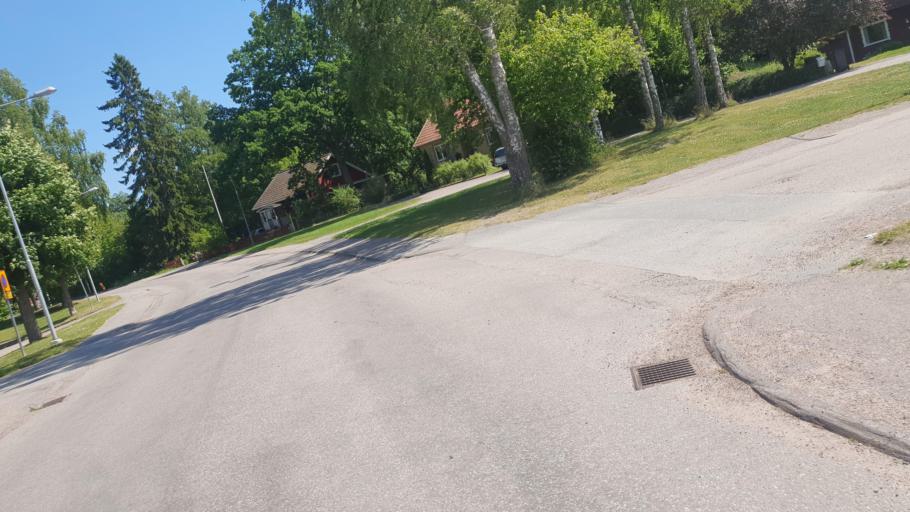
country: SE
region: Uppsala
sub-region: Osthammars Kommun
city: Gimo
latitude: 60.1720
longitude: 18.1772
